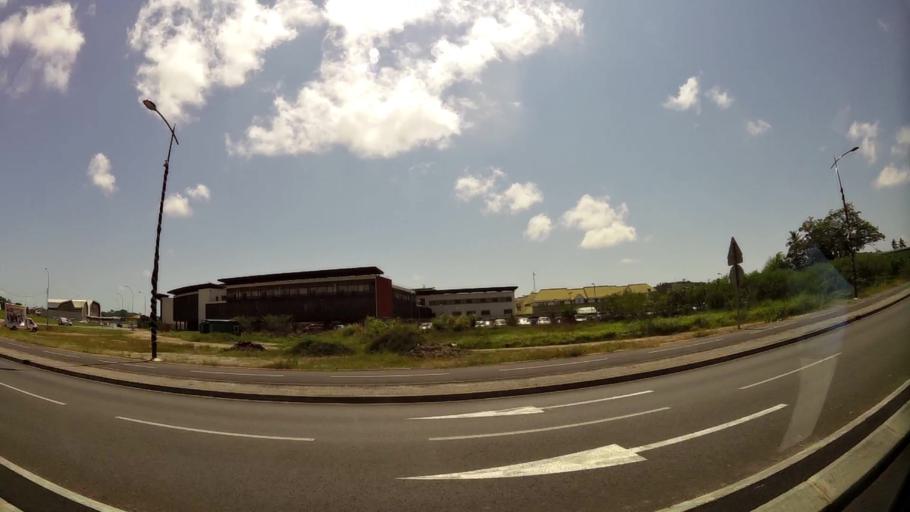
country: GF
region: Guyane
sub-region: Guyane
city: Cayenne
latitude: 4.9231
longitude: -52.3239
